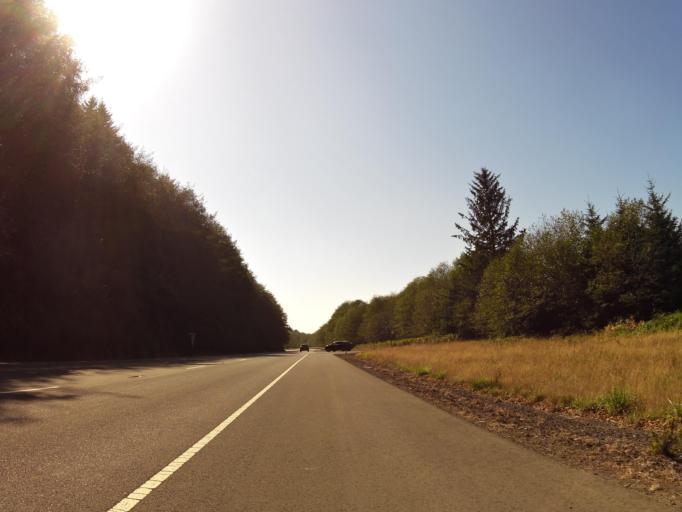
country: US
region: Oregon
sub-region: Tillamook County
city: Pacific City
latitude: 45.1474
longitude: -123.9630
